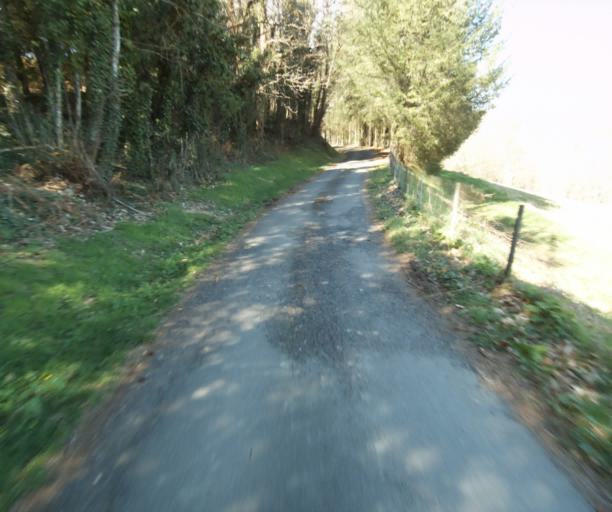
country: FR
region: Limousin
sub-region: Departement de la Correze
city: Chameyrat
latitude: 45.2771
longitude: 1.7042
